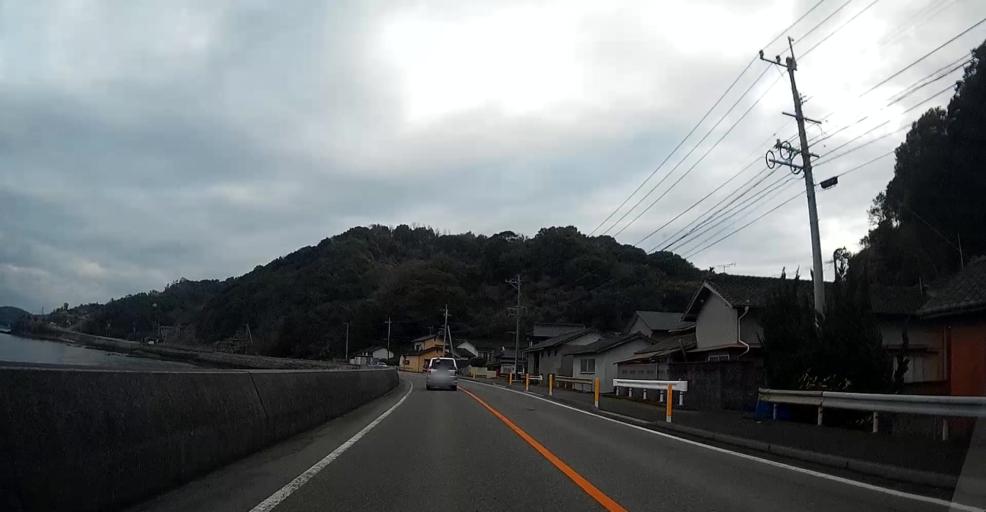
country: JP
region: Kumamoto
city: Hondo
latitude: 32.4840
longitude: 130.2804
